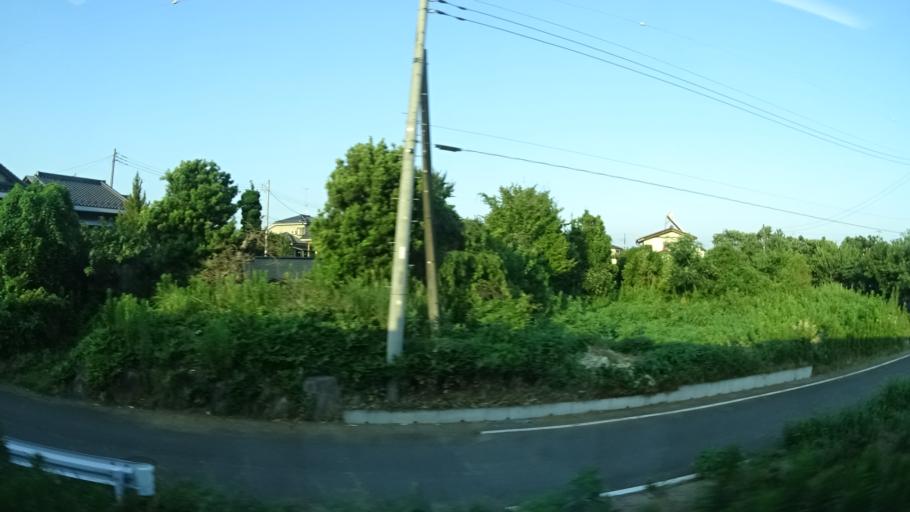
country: JP
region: Ibaraki
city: Ishioka
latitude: 36.2418
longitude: 140.2883
